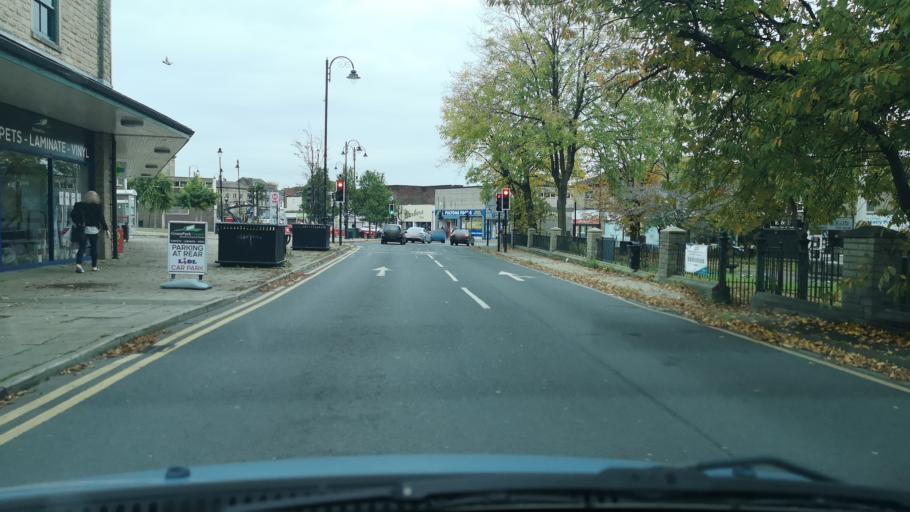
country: GB
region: England
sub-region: Kirklees
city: Heckmondwike
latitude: 53.7082
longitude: -1.6765
